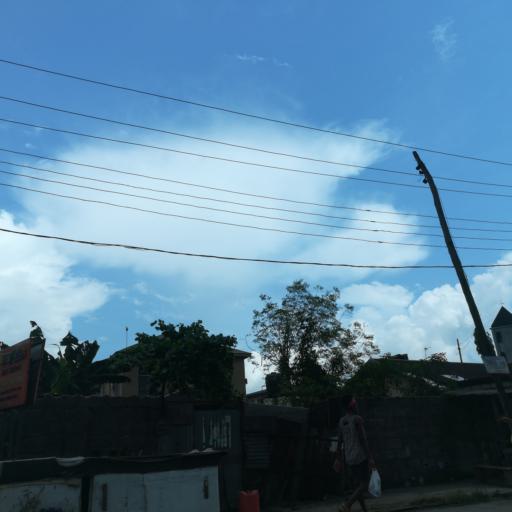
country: NG
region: Rivers
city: Port Harcourt
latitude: 4.8124
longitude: 7.0592
